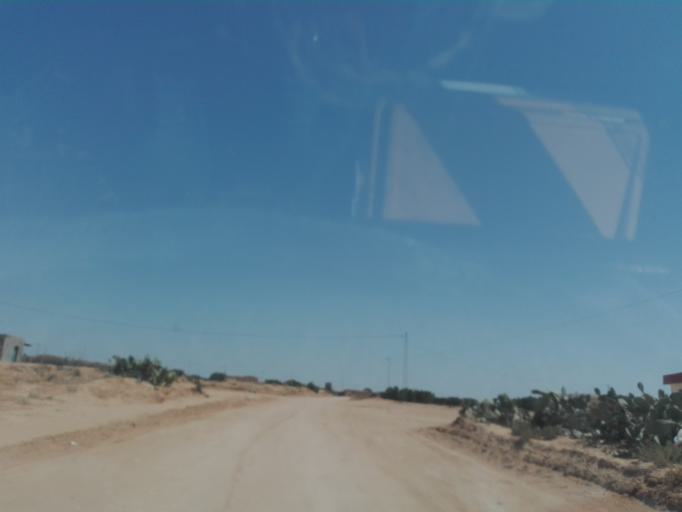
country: TN
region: Safaqis
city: Bi'r `Ali Bin Khalifah
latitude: 34.6650
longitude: 10.2385
